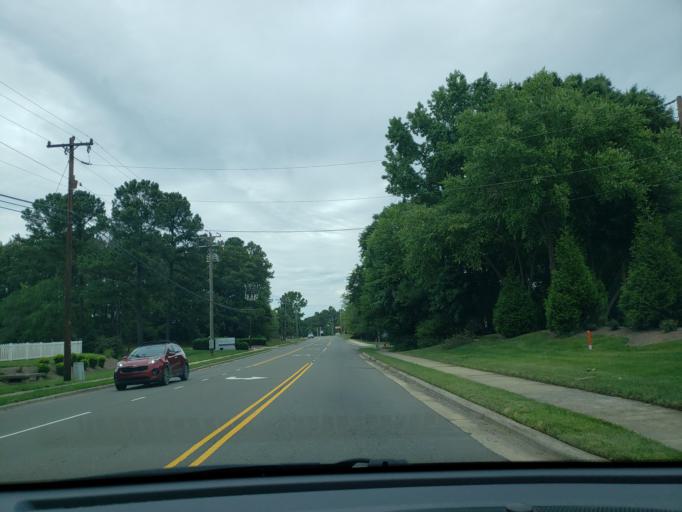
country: US
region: North Carolina
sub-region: Orange County
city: Chapel Hill
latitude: 35.9085
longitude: -78.9837
